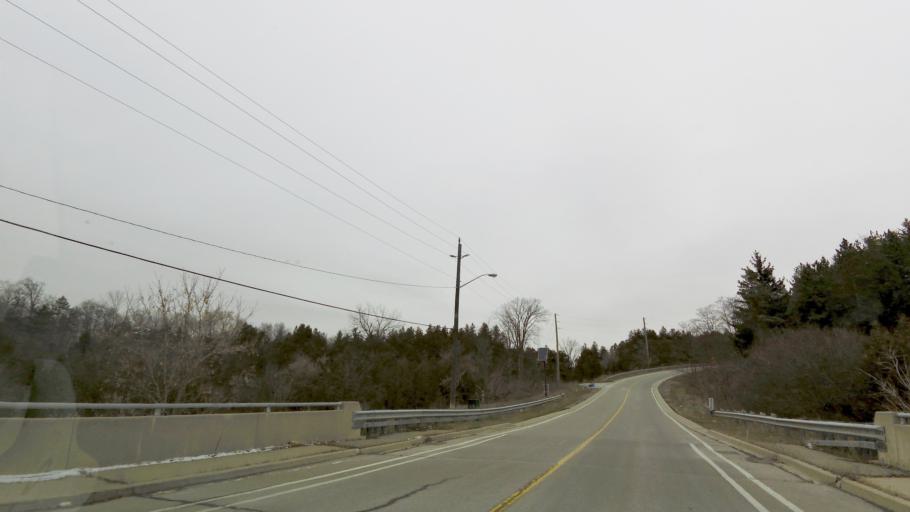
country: CA
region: Ontario
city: Vaughan
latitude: 43.8457
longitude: -79.6251
